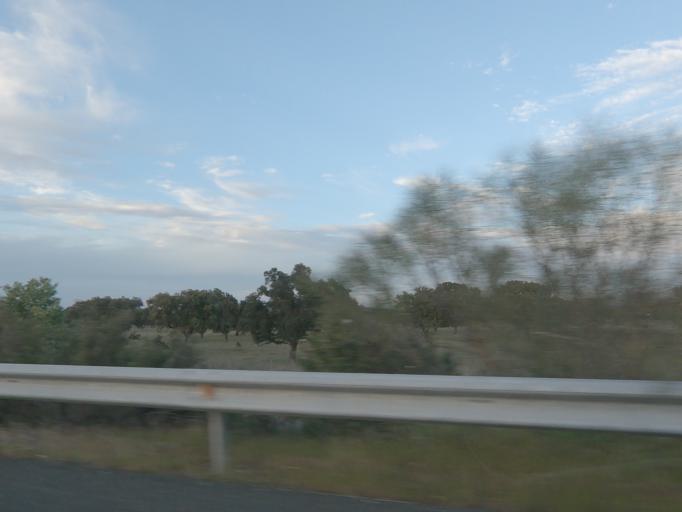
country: ES
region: Extremadura
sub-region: Provincia de Caceres
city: Casas de Don Antonio
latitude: 39.2013
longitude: -6.2813
